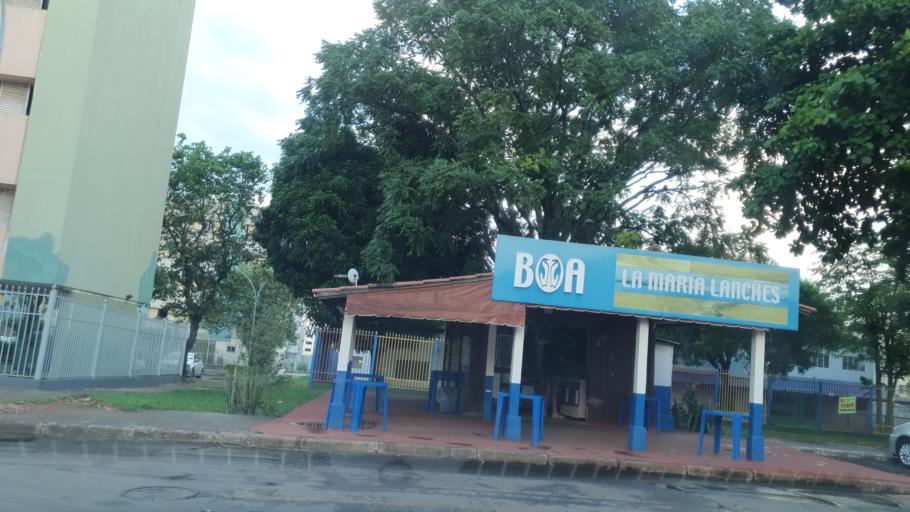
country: BR
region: Federal District
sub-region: Brasilia
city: Brasilia
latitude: -15.7944
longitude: -47.9362
